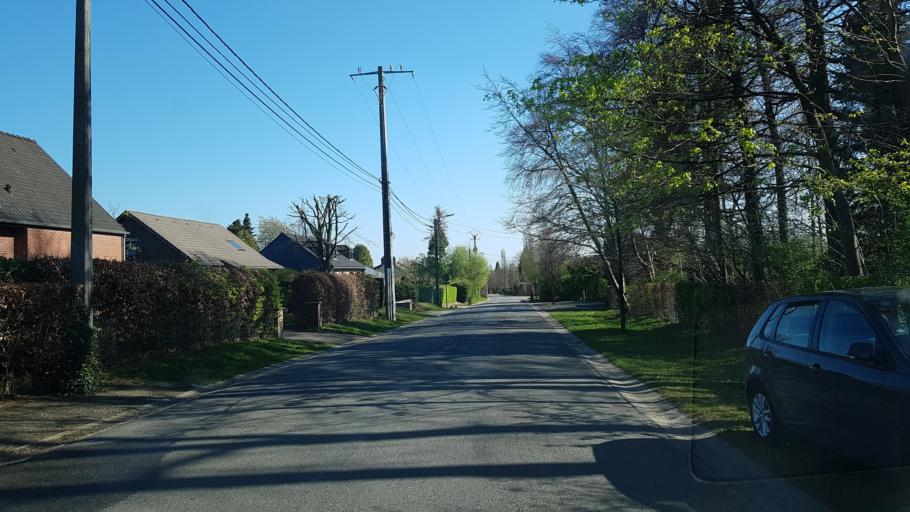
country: BE
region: Wallonia
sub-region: Province de Liege
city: Spa
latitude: 50.4742
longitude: 5.8465
